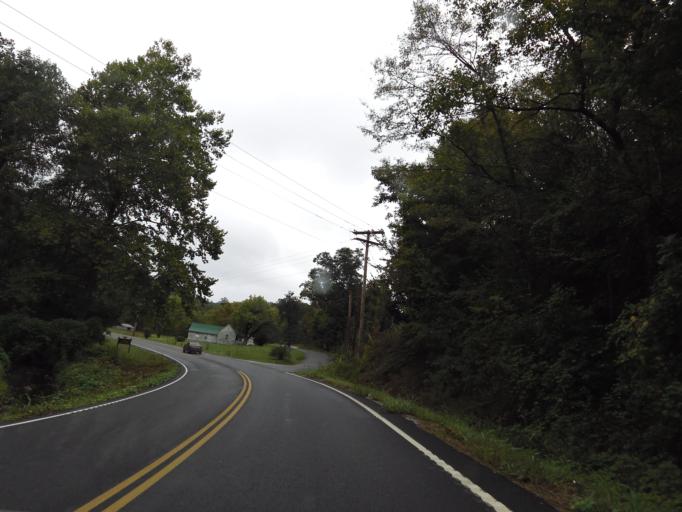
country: US
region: Tennessee
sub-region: Bradley County
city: Cleveland
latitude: 35.1781
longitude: -84.9880
